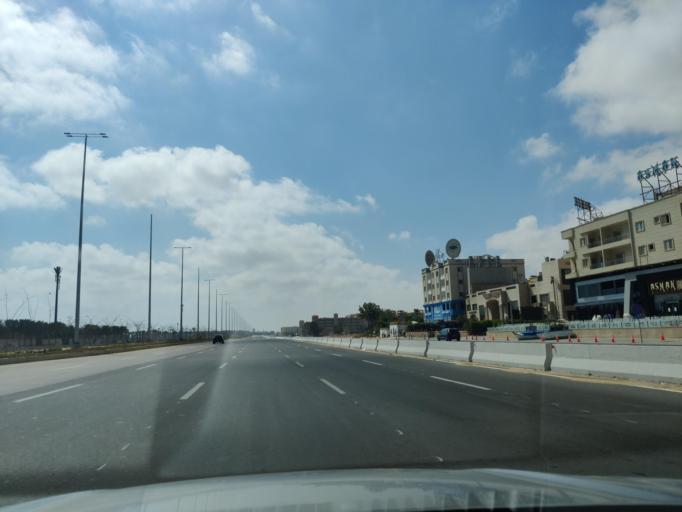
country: EG
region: Muhafazat Matruh
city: Al `Alamayn
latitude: 30.9632
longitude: 28.7531
